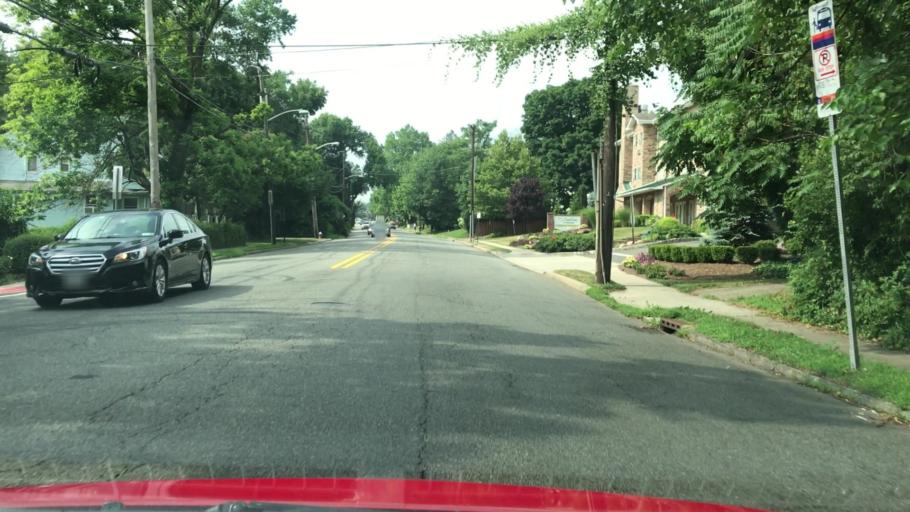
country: US
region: New Jersey
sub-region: Bergen County
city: Bogota
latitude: 40.8780
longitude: -74.0111
